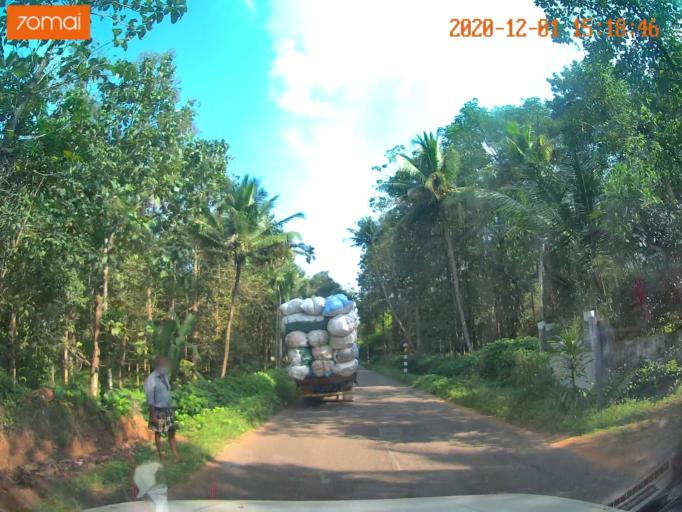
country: IN
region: Kerala
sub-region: Ernakulam
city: Ramamangalam
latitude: 9.9360
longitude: 76.5329
